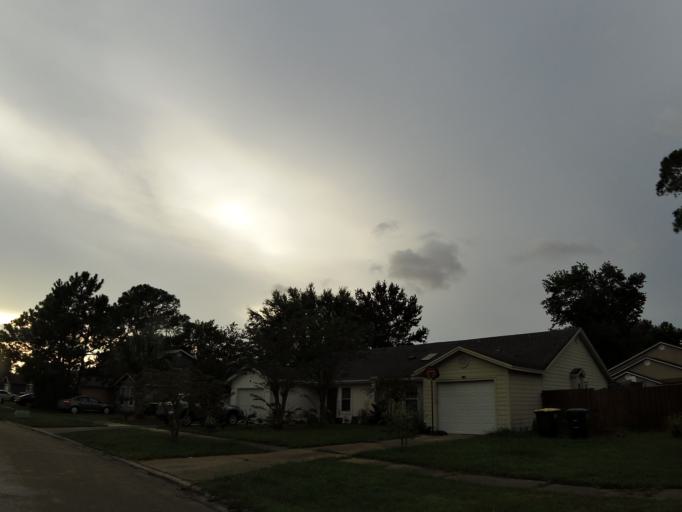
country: US
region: Florida
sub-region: Duval County
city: Neptune Beach
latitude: 30.3022
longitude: -81.5147
